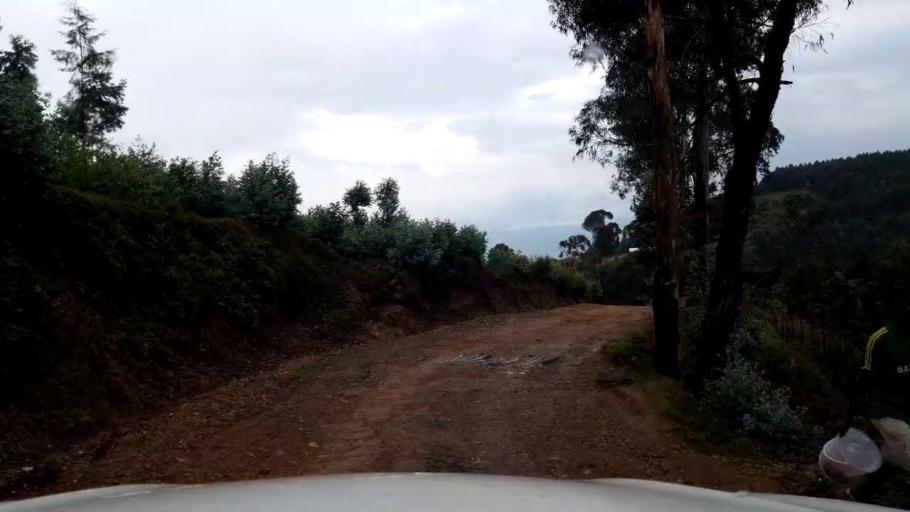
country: RW
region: Western Province
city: Kibuye
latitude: -2.0225
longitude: 29.4566
